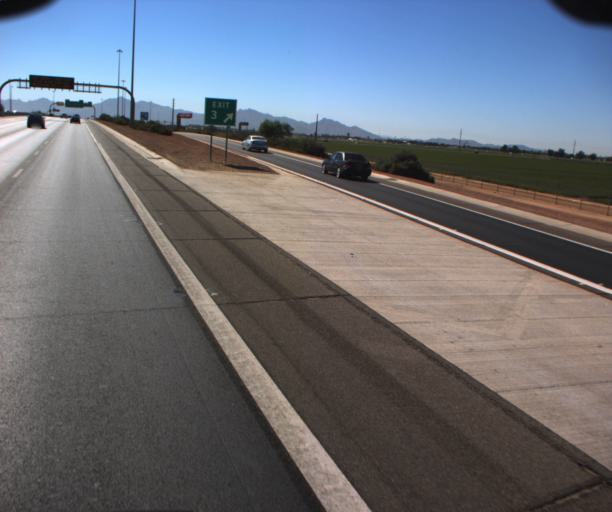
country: US
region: Arizona
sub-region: Maricopa County
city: Tolleson
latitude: 33.4836
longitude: -112.2640
